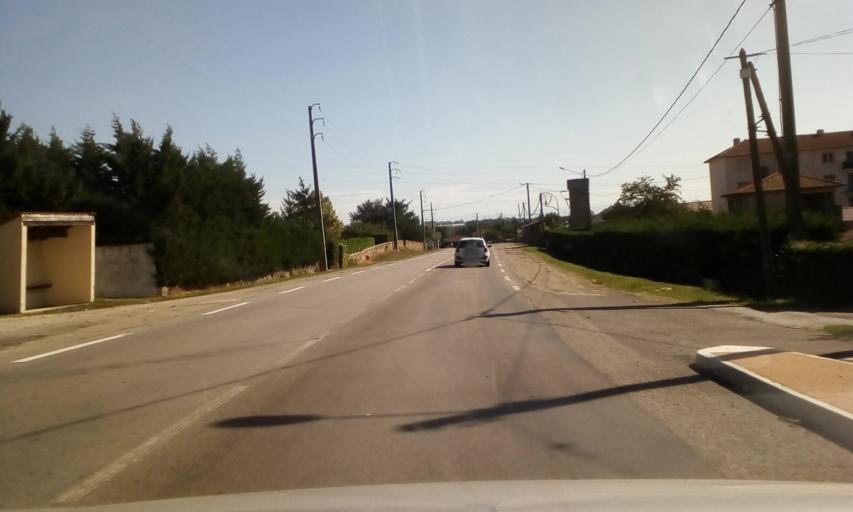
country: FR
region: Rhone-Alpes
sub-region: Departement de l'Ardeche
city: Boulieu-les-Annonay
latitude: 45.2559
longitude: 4.6730
